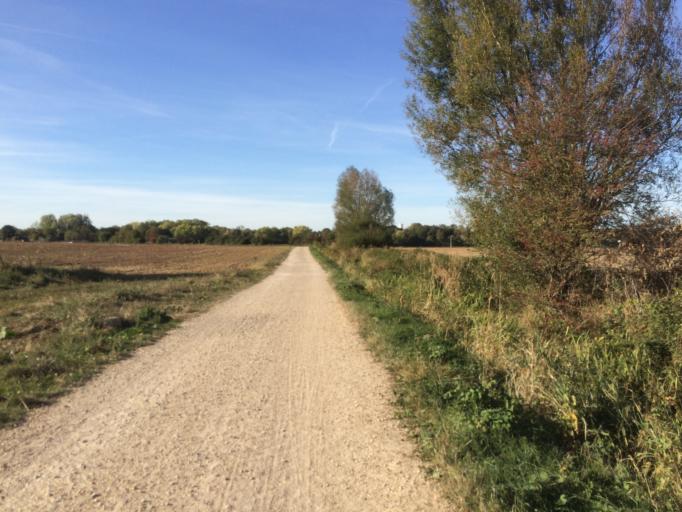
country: FR
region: Ile-de-France
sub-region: Departement de l'Essonne
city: Saclay
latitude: 48.7322
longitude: 2.1795
